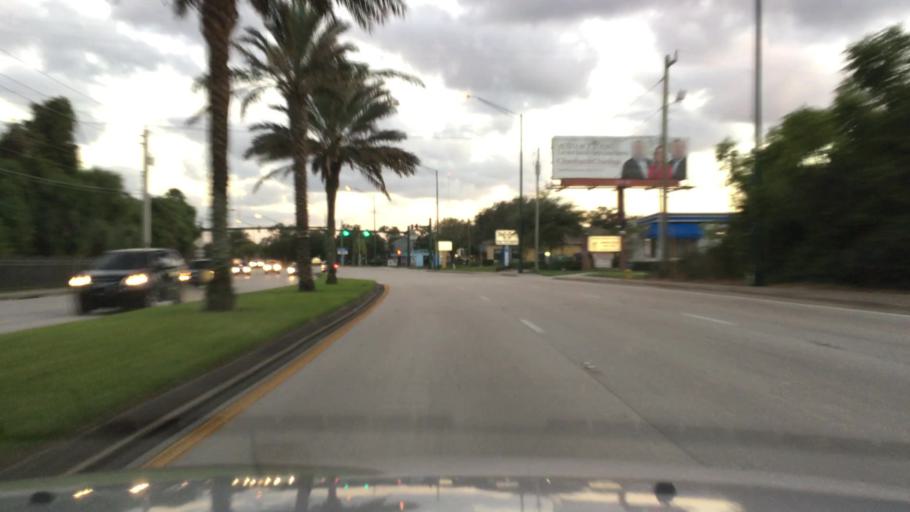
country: US
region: Florida
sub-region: Volusia County
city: Ormond Beach
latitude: 29.2751
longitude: -81.0830
